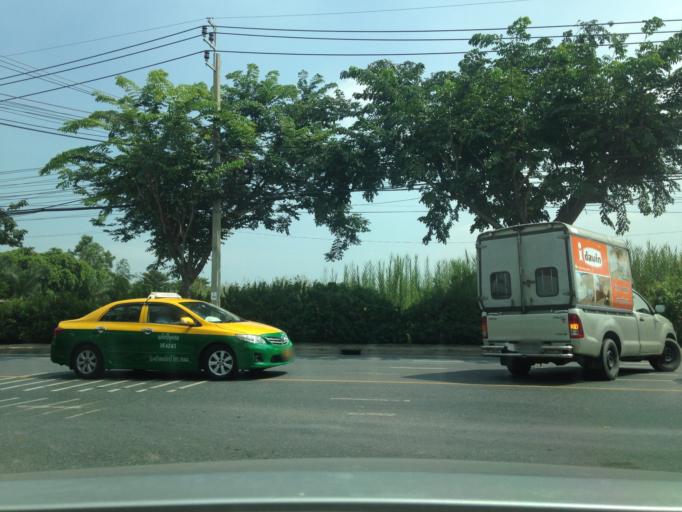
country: TH
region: Bangkok
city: Lat Phrao
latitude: 13.8305
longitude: 100.6233
